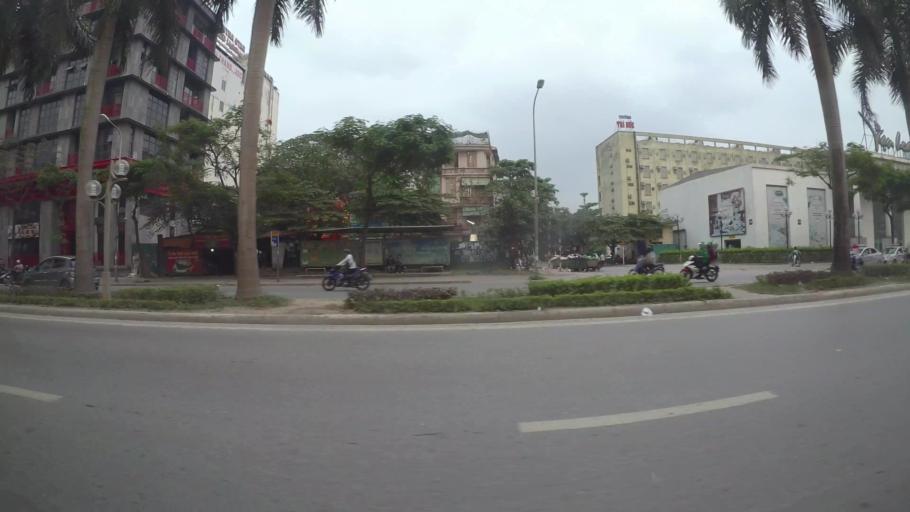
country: VN
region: Ha Noi
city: Cau Dien
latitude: 21.0312
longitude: 105.7693
